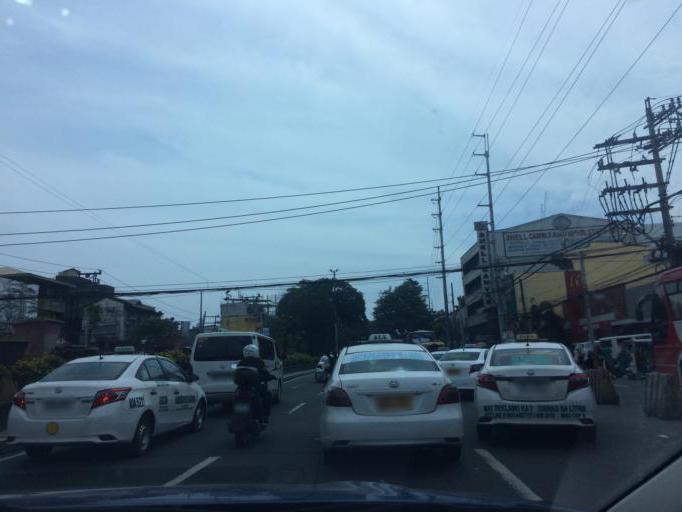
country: PH
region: Metro Manila
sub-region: Makati City
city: Makati City
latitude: 14.5541
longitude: 120.9968
